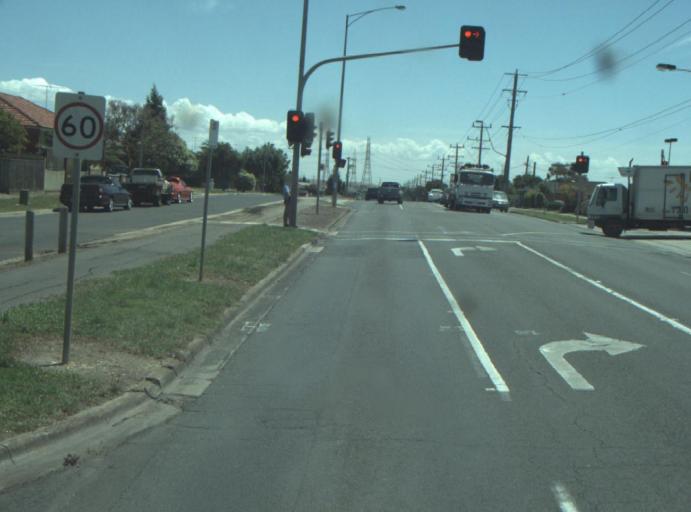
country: AU
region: Victoria
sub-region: Greater Geelong
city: Bell Post Hill
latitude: -38.0903
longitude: 144.3354
